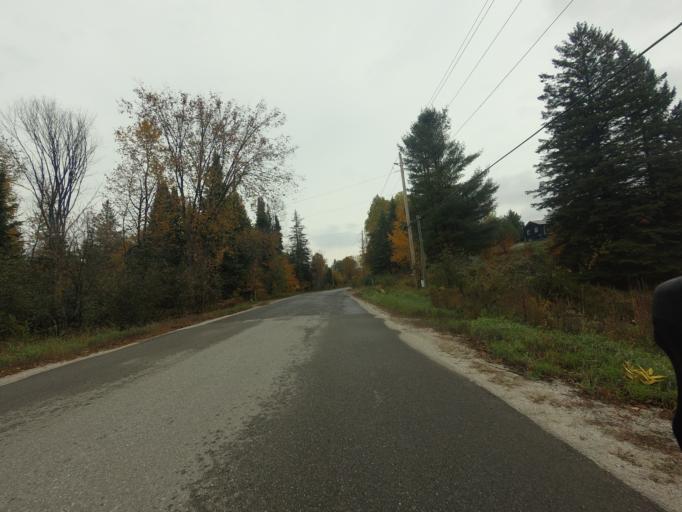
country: CA
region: Ontario
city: Perth
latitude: 45.1166
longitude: -76.5054
